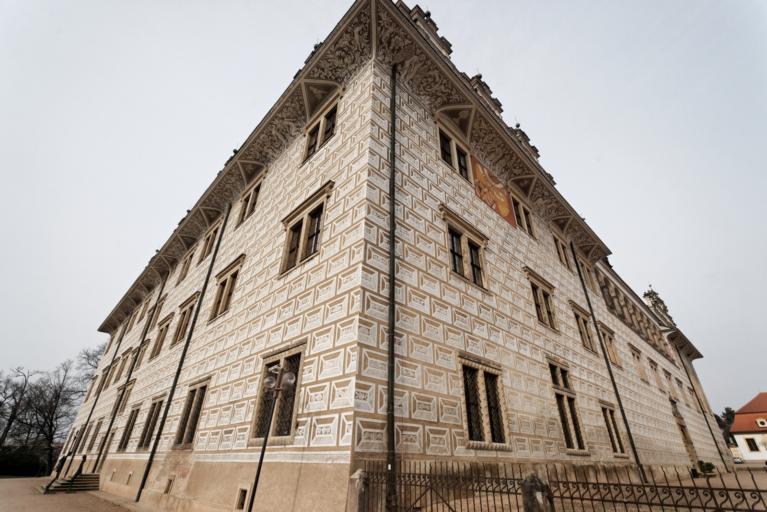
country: CZ
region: Pardubicky
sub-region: Okres Svitavy
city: Litomysl
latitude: 49.8730
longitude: 16.3127
